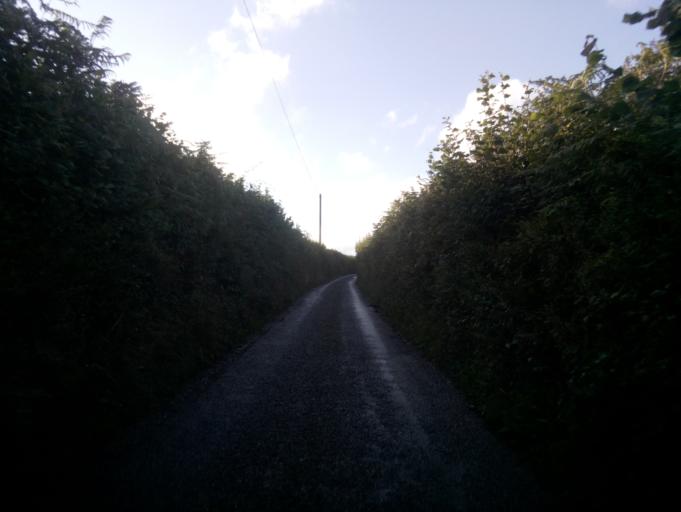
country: GB
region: England
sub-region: Devon
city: Dartmouth
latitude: 50.3415
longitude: -3.6082
